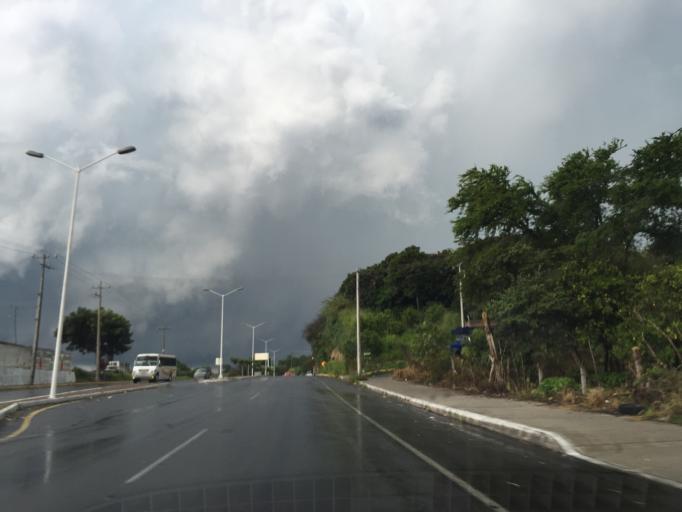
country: MX
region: Colima
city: Queseria
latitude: 19.3837
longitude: -103.5721
